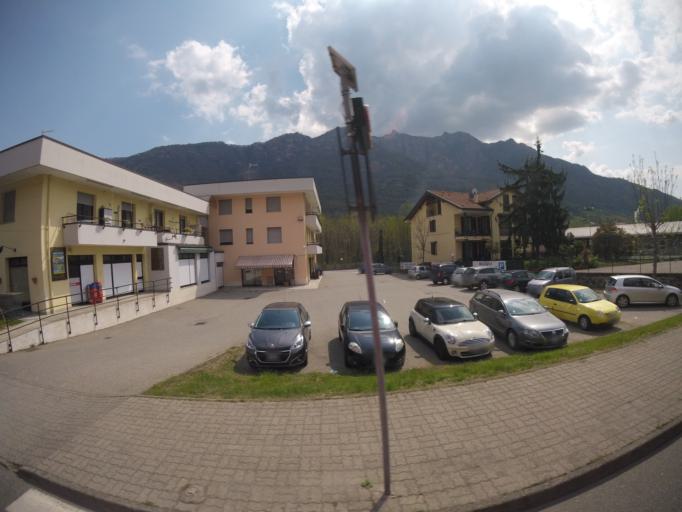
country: IT
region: Piedmont
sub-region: Provincia Verbano-Cusio-Ossola
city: Gabbio-Cereda-Ramate
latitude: 45.9020
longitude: 8.4177
